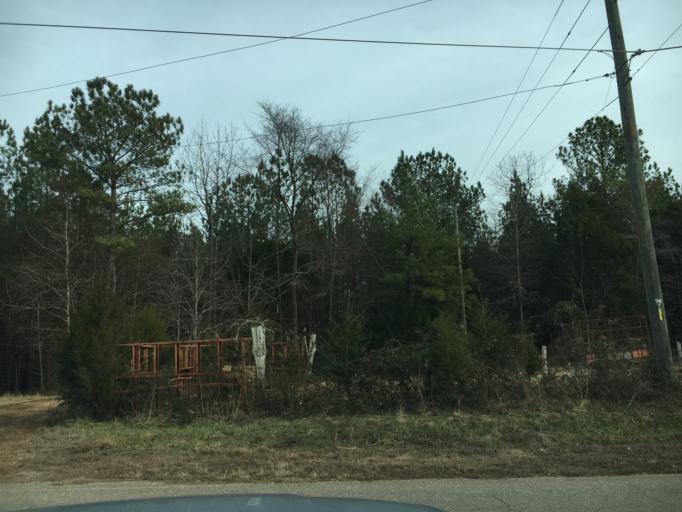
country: US
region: South Carolina
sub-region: Laurens County
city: Clinton
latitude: 34.4779
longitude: -81.8227
